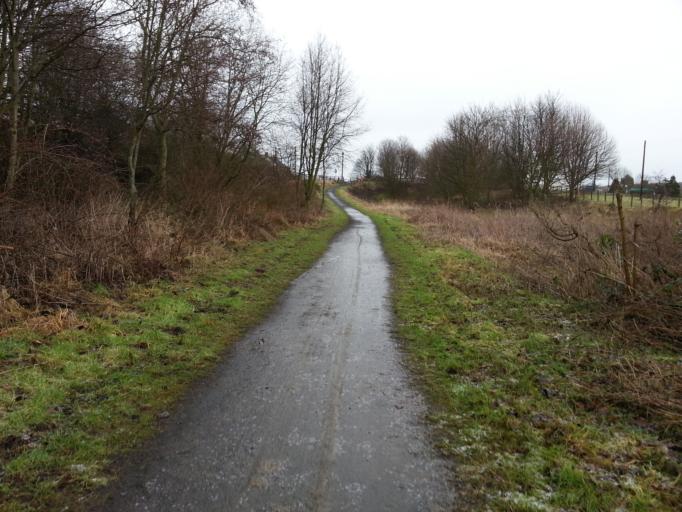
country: GB
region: England
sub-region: County Durham
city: Crook
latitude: 54.7589
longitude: -1.7293
